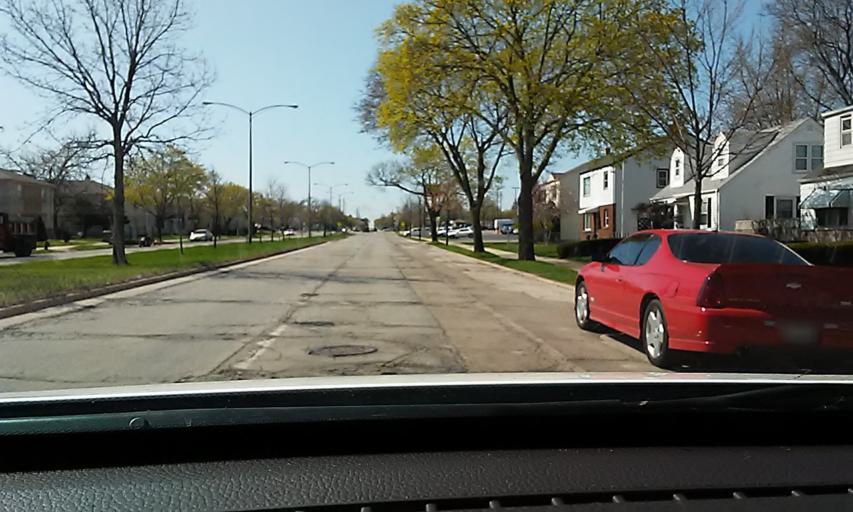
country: US
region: Wisconsin
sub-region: Milwaukee County
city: West Milwaukee
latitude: 42.9906
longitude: -87.9878
